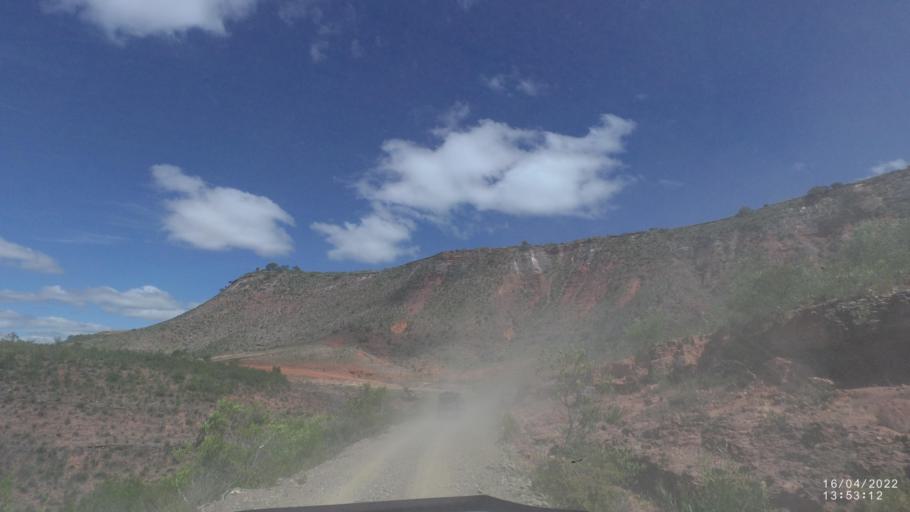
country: BO
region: Cochabamba
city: Mizque
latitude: -18.0231
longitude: -65.5715
